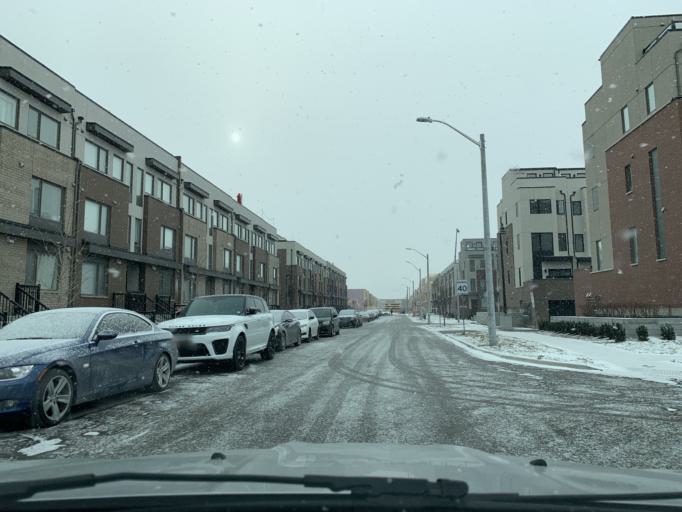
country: CA
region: Ontario
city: Concord
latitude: 43.7374
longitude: -79.4760
